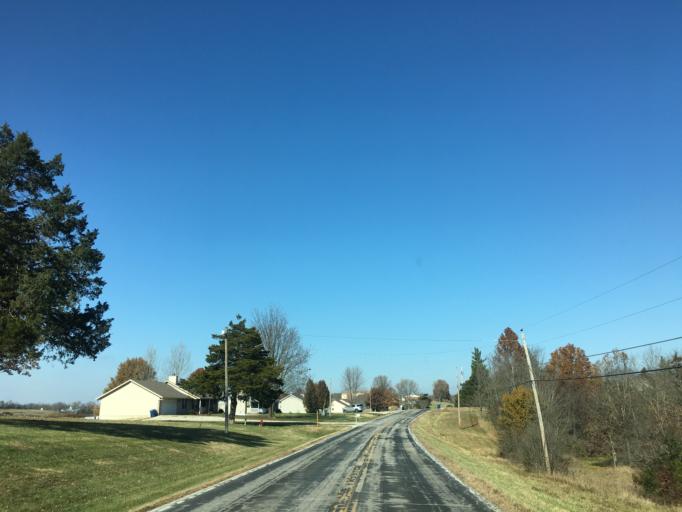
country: US
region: Missouri
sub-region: Cole County
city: Wardsville
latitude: 38.4703
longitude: -92.1770
